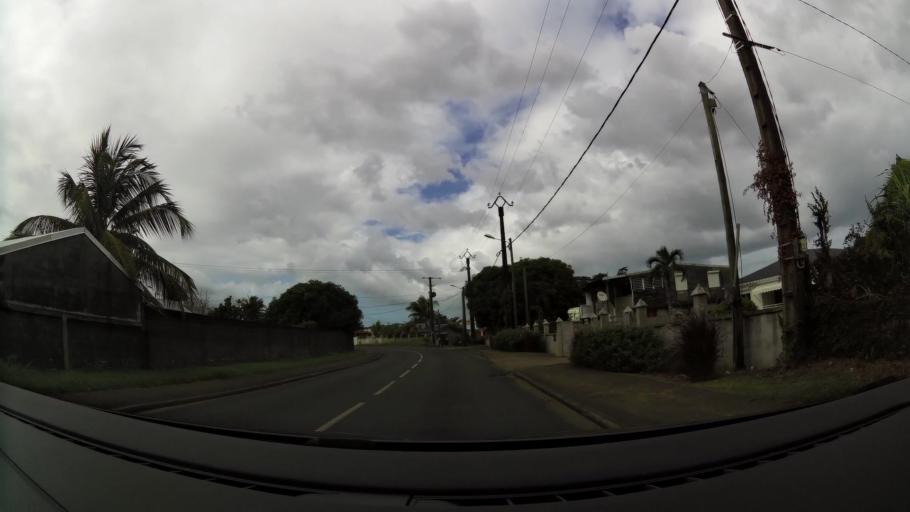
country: GP
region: Guadeloupe
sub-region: Guadeloupe
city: Lamentin
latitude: 16.2640
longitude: -61.6242
